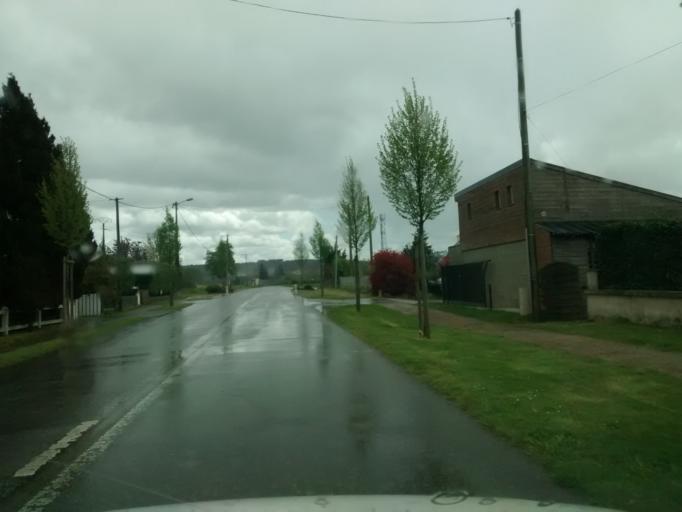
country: FR
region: Brittany
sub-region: Departement du Morbihan
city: Pleucadeuc
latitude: 47.7679
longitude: -2.3177
